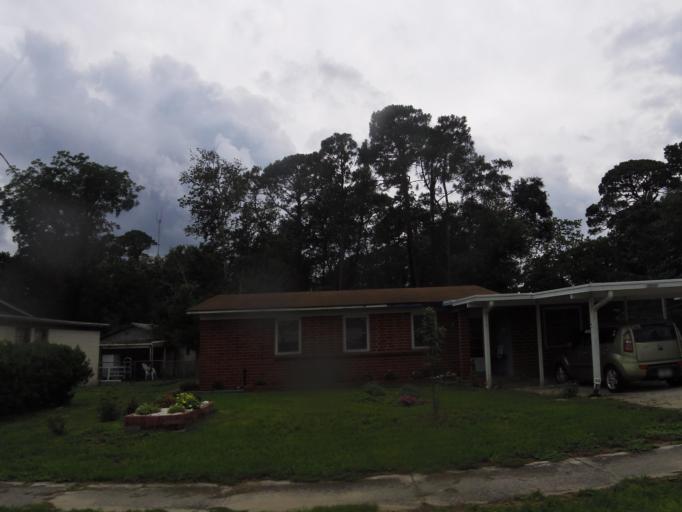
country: US
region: Florida
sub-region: Duval County
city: Jacksonville
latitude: 30.2772
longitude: -81.5432
